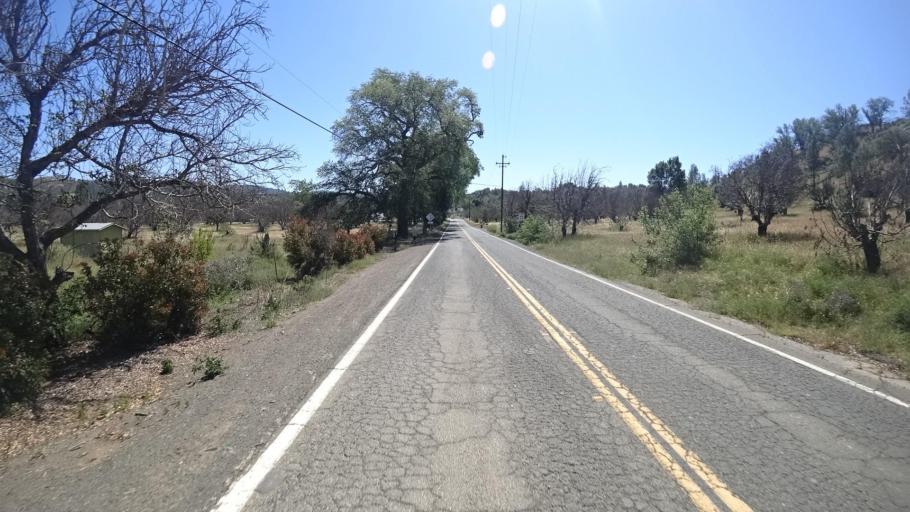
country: US
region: California
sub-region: Lake County
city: Lower Lake
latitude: 38.9088
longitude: -122.5892
